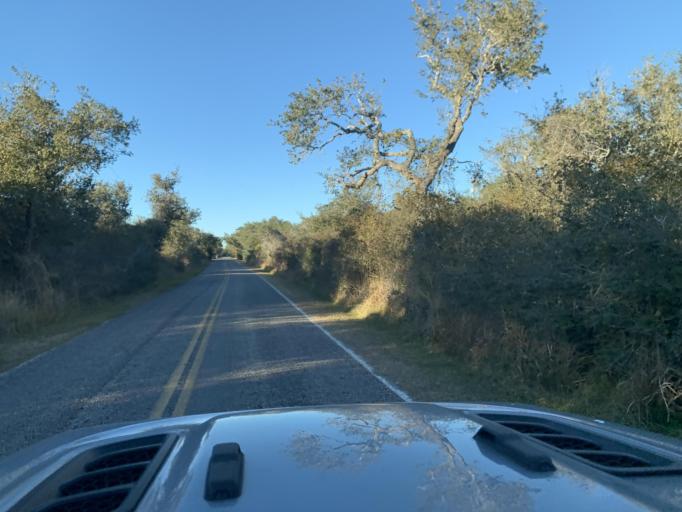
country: US
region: Texas
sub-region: Aransas County
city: Fulton
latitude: 28.1499
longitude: -96.9843
